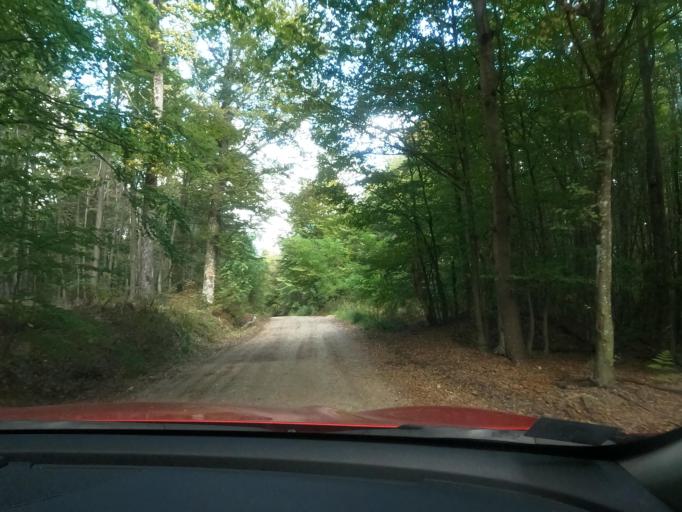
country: BA
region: Federation of Bosnia and Herzegovina
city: Velika Kladusa
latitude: 45.2680
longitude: 15.7780
